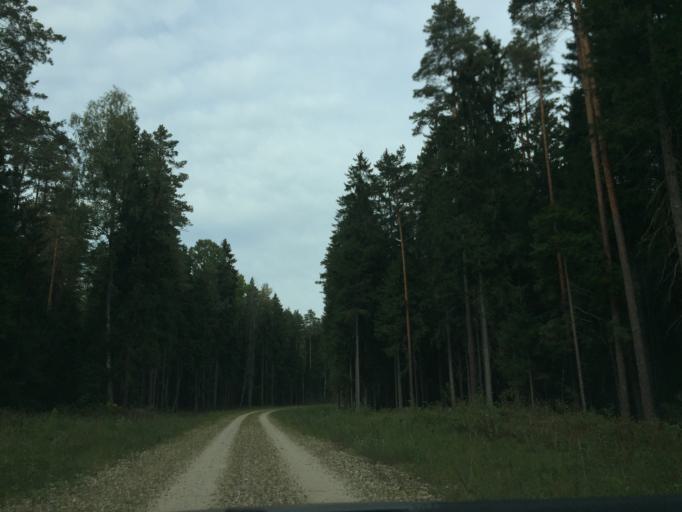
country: LV
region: Baldone
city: Baldone
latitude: 56.7518
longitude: 24.4669
